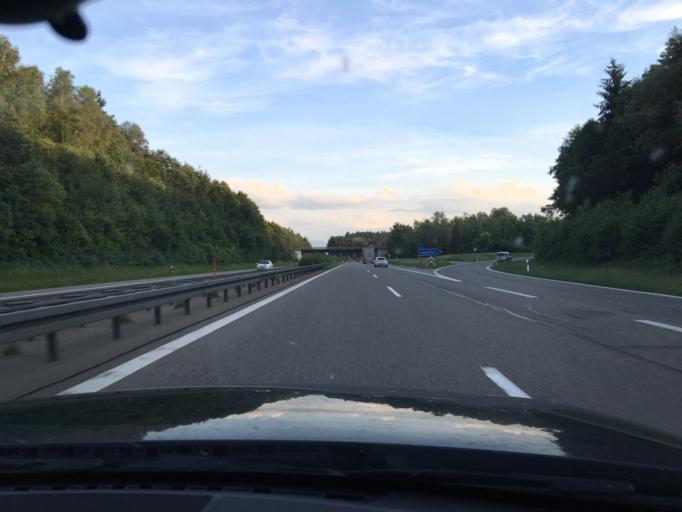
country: DE
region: Bavaria
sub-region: Swabia
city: Weissensberg
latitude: 47.5819
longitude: 9.7355
